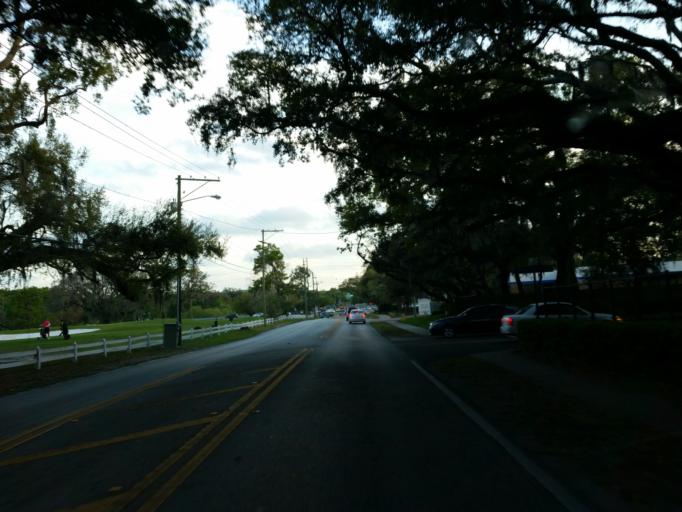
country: US
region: Florida
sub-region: Hillsborough County
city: University
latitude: 28.0715
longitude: -82.4100
